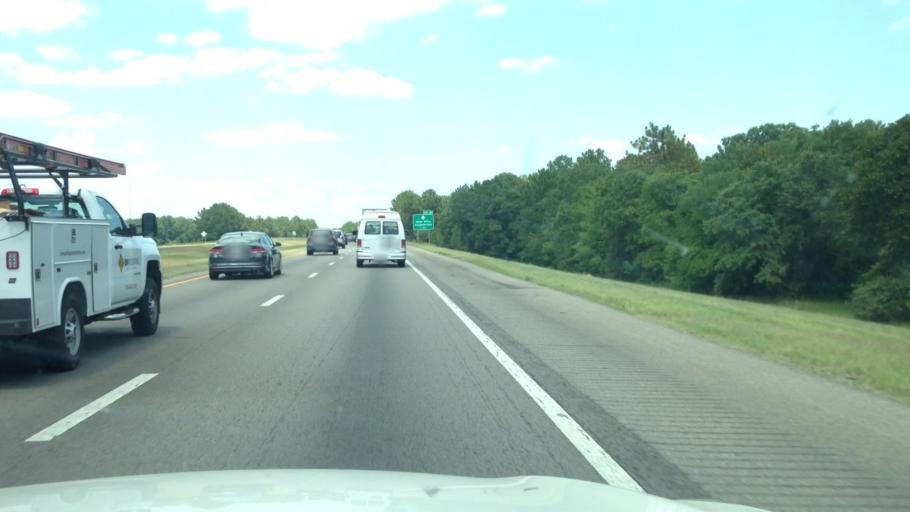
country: US
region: North Carolina
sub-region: Cumberland County
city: Hope Mills
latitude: 34.9263
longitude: -78.9420
